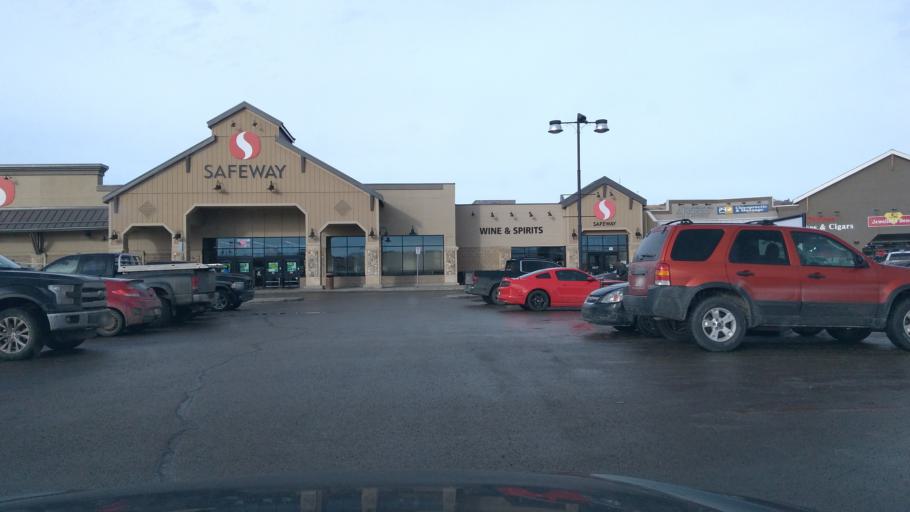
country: CA
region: Alberta
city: Cochrane
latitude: 51.1847
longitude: -114.4761
